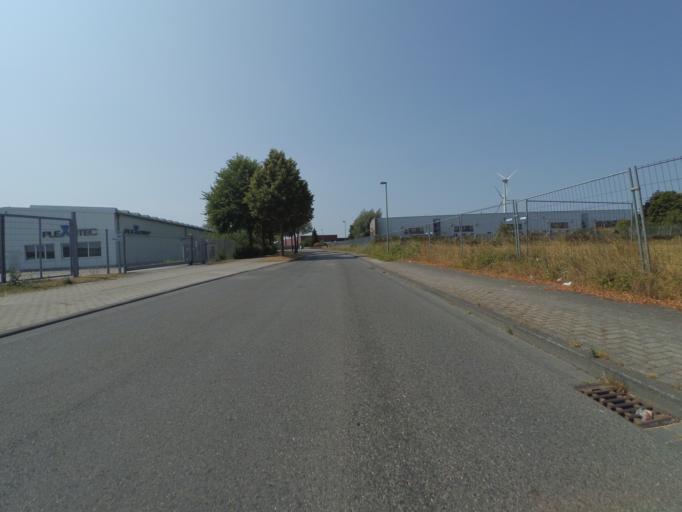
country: DE
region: North Rhine-Westphalia
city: Rees
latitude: 51.7802
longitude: 6.4080
